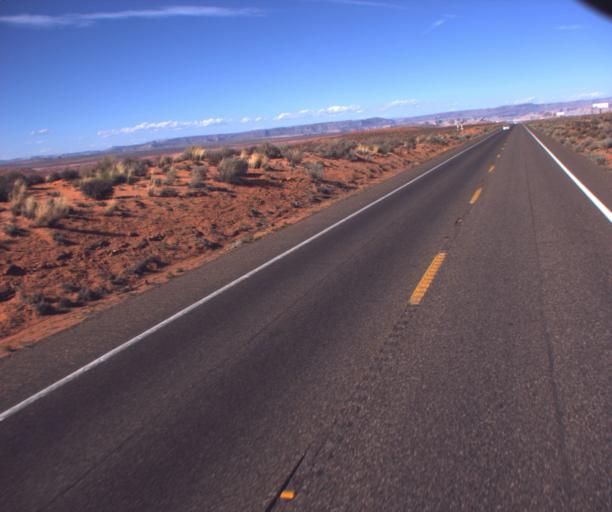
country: US
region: Arizona
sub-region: Coconino County
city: Page
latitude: 36.8616
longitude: -111.5050
